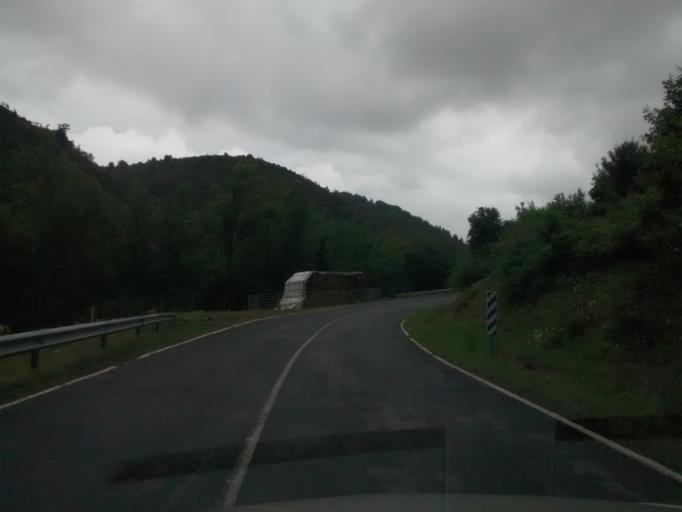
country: ES
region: La Rioja
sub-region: Provincia de La Rioja
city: Ajamil
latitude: 42.1713
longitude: -2.4853
